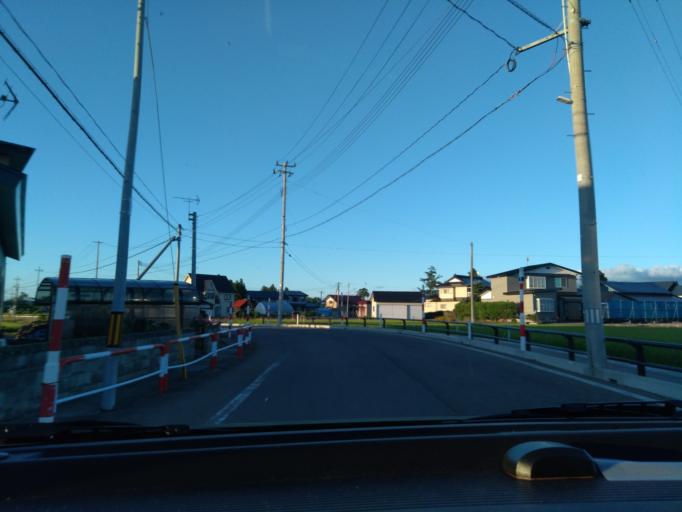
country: JP
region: Akita
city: Omagari
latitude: 39.4842
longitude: 140.5323
